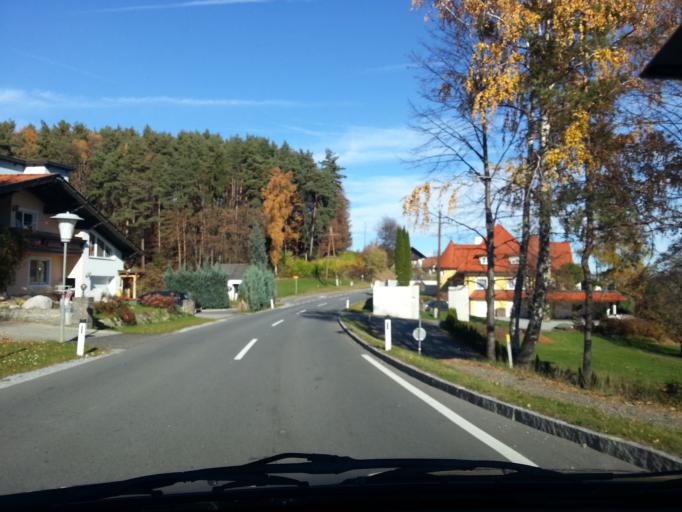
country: AT
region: Styria
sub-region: Politischer Bezirk Deutschlandsberg
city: Gundersdorf
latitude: 46.9521
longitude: 15.2317
